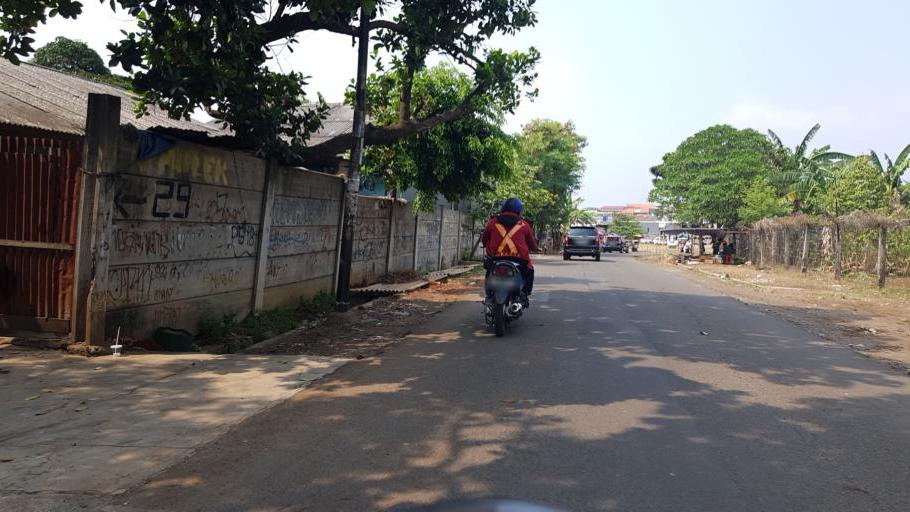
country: ID
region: West Java
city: Bekasi
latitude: -6.2864
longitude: 106.9289
